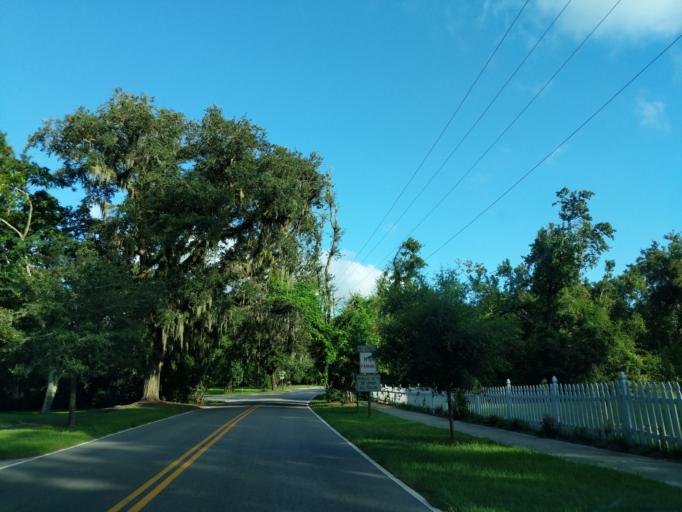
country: US
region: South Carolina
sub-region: Charleston County
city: Awendaw
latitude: 33.0923
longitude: -79.4644
